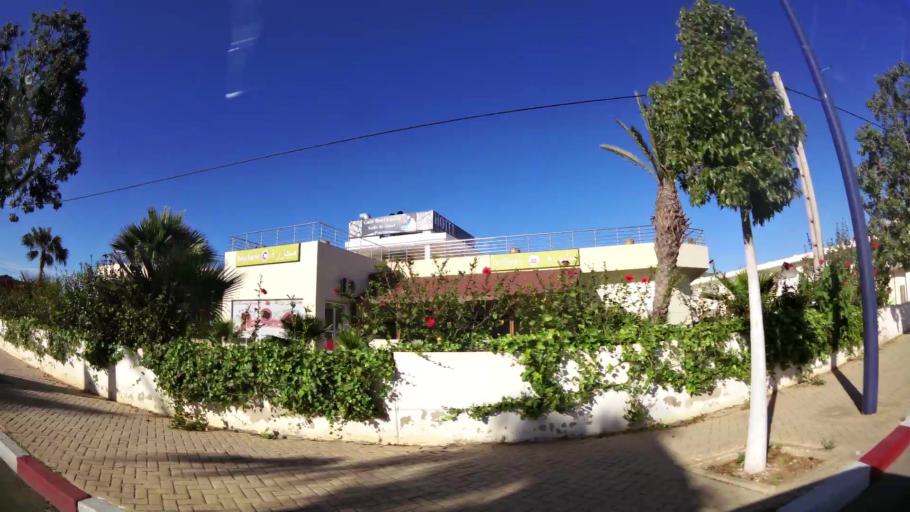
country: MA
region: Oriental
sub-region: Berkane-Taourirt
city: Madagh
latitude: 35.0676
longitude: -2.2163
